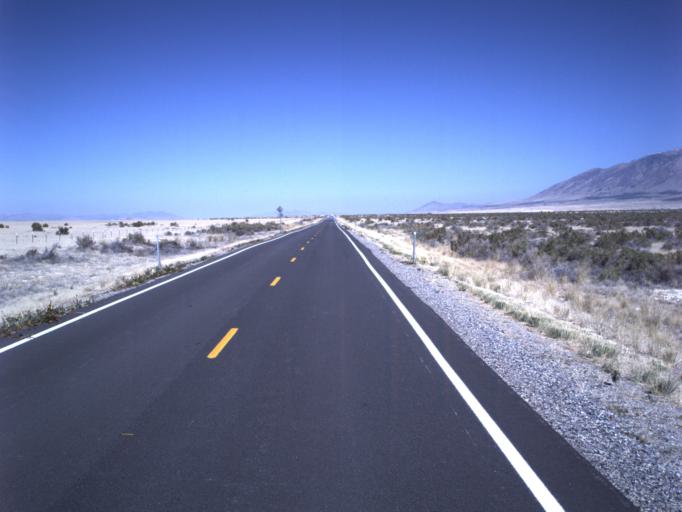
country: US
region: Utah
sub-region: Tooele County
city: Grantsville
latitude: 40.2623
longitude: -112.7408
